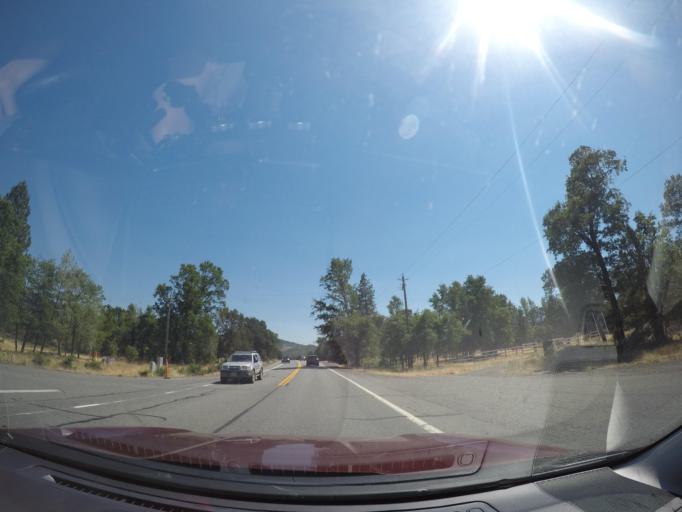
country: US
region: California
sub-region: Shasta County
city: Burney
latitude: 40.8055
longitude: -121.9403
